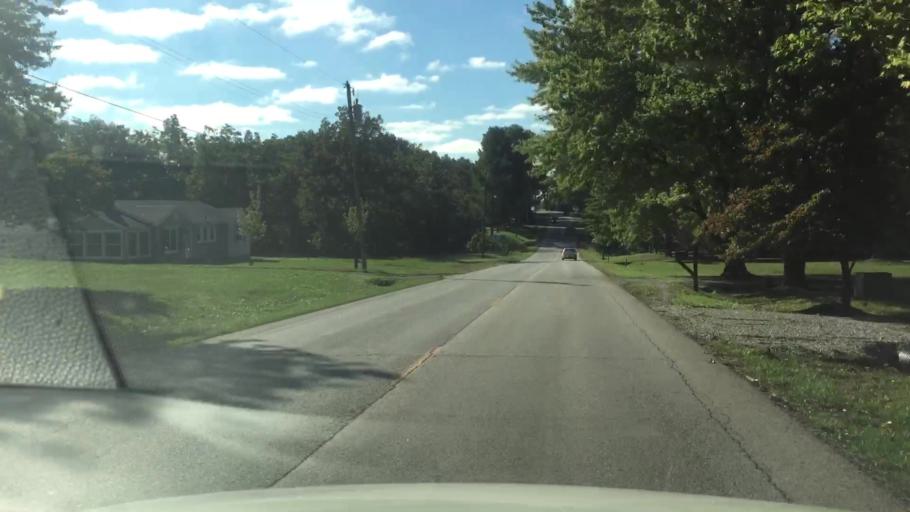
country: US
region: Missouri
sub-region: Howard County
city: New Franklin
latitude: 39.0219
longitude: -92.7459
